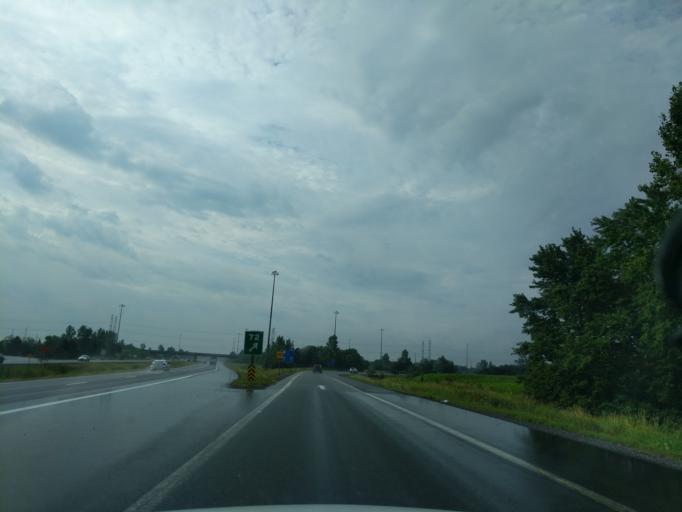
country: CA
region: Ontario
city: Bells Corners
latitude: 45.3166
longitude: -75.8049
